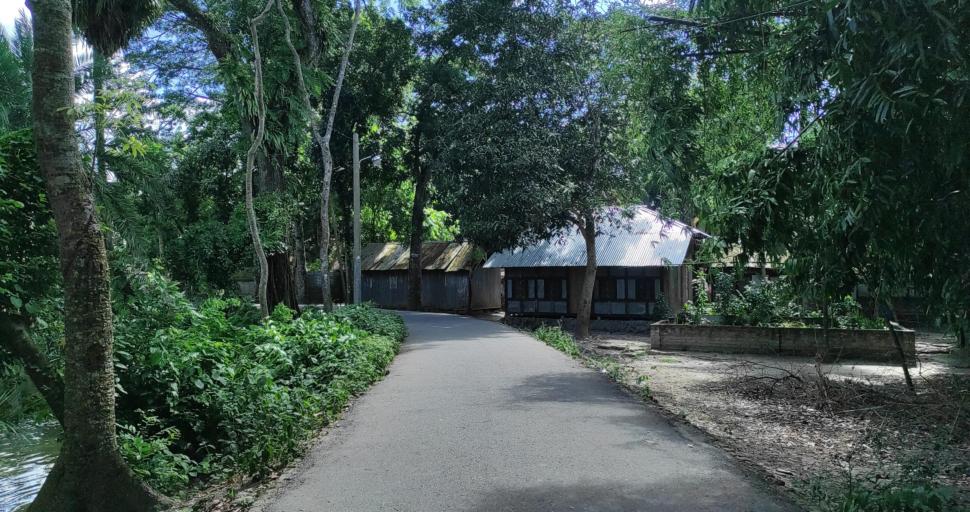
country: BD
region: Barisal
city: Gaurnadi
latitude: 22.9897
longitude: 90.2213
